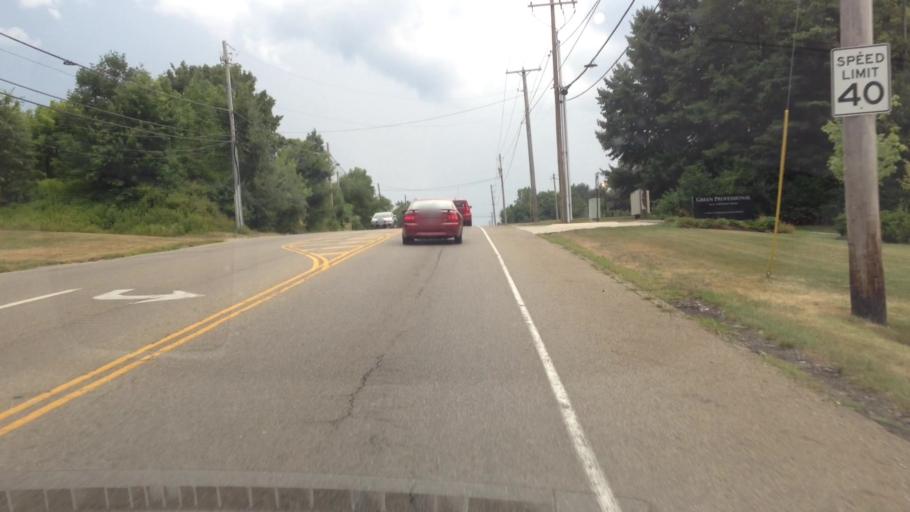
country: US
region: Ohio
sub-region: Summit County
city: Green
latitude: 40.9733
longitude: -81.4647
